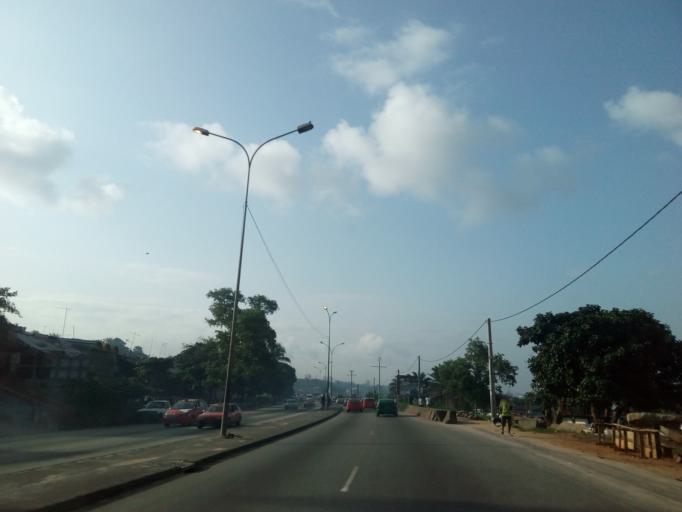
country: CI
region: Lagunes
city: Abidjan
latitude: 5.3456
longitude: -4.0388
